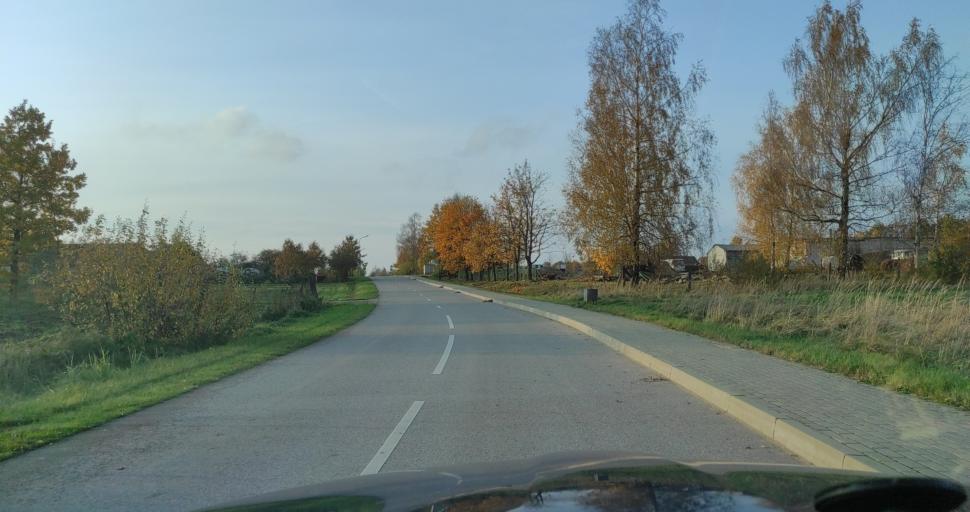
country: LV
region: Vainode
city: Vainode
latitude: 56.4202
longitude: 21.8523
